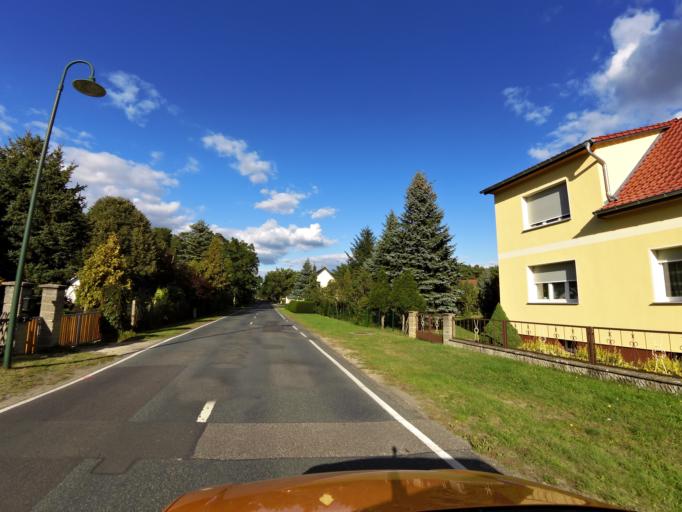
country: DE
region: Brandenburg
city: Luckenwalde
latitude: 52.1298
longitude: 13.1692
